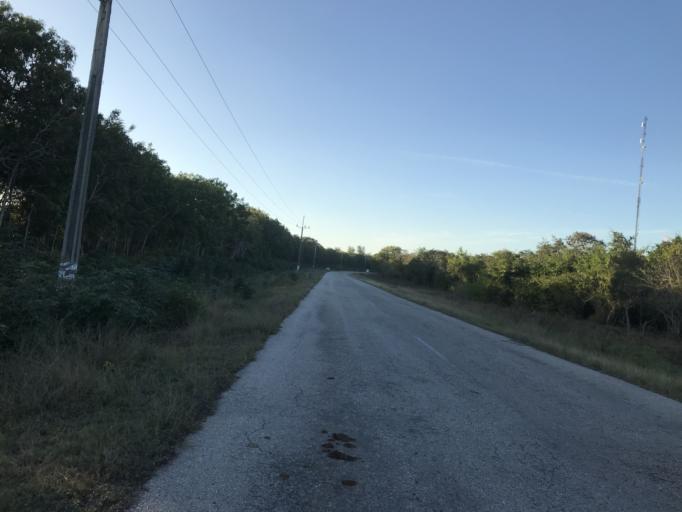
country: CU
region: Cienfuegos
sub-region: Municipio de Aguada de Pasajeros
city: Aguada de Pasajeros
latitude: 22.0686
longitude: -81.0504
